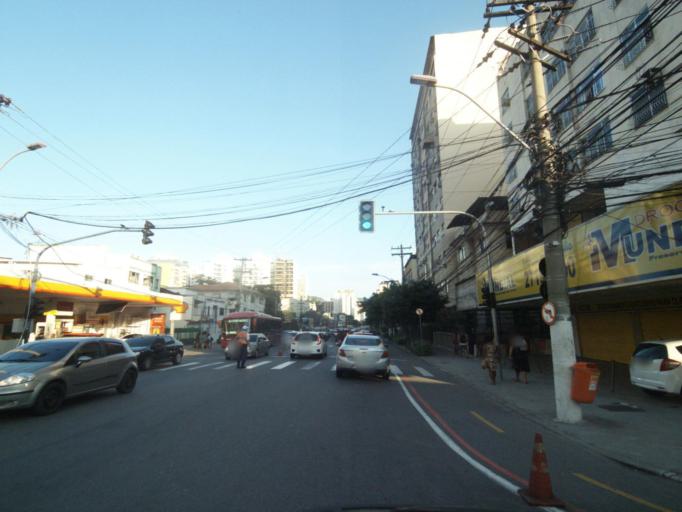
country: BR
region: Rio de Janeiro
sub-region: Niteroi
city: Niteroi
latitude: -22.8994
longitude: -43.1108
